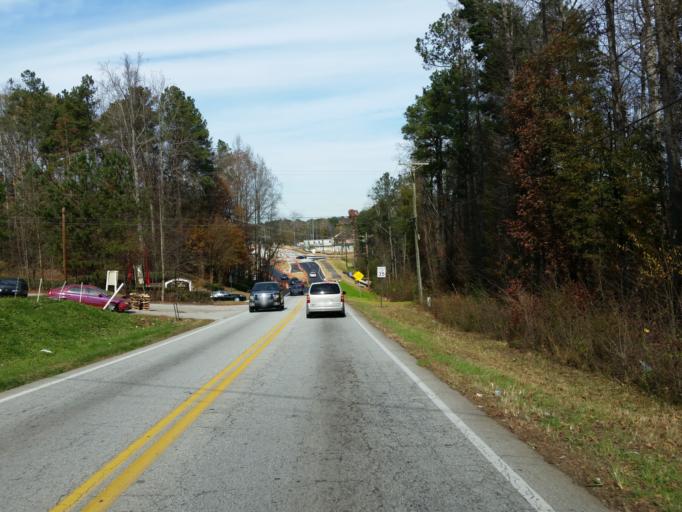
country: US
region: Georgia
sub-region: Douglas County
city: Lithia Springs
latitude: 33.7634
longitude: -84.6509
